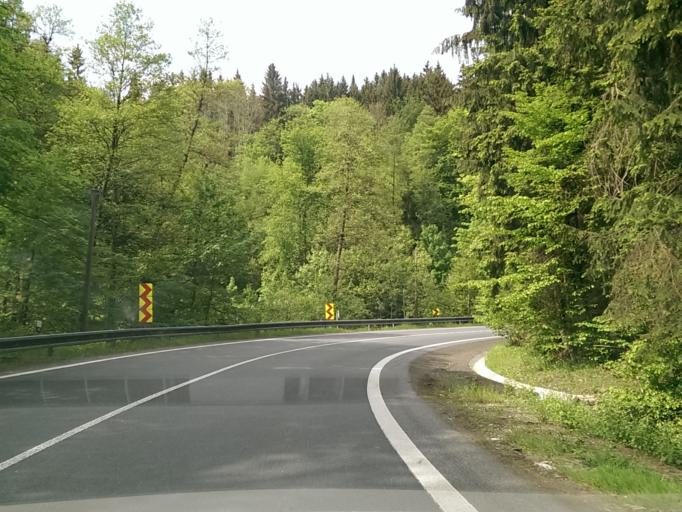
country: CZ
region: Liberecky
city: Zelezny Brod
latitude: 50.6541
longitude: 15.2535
